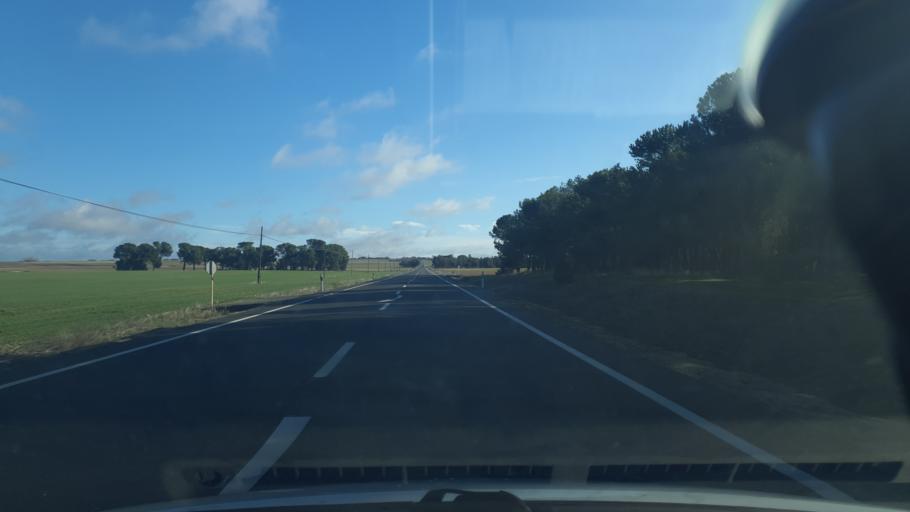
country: ES
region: Castille and Leon
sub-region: Provincia de Segovia
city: Martin Munoz de la Dehesa
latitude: 41.0465
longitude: -4.6590
